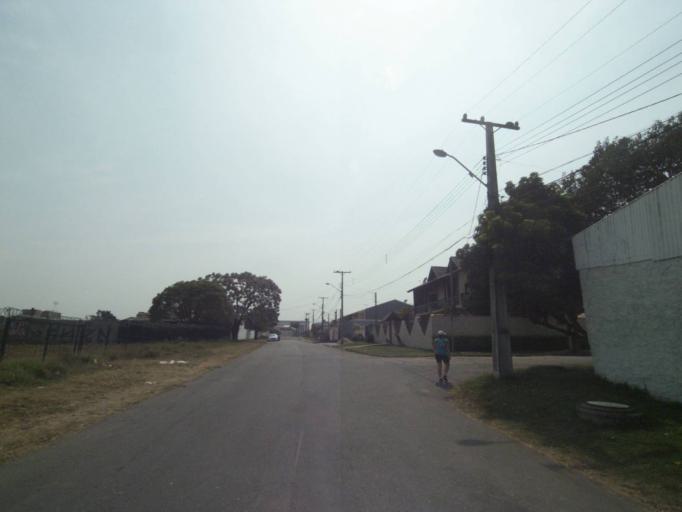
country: BR
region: Parana
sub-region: Sao Jose Dos Pinhais
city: Sao Jose dos Pinhais
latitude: -25.4894
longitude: -49.2160
